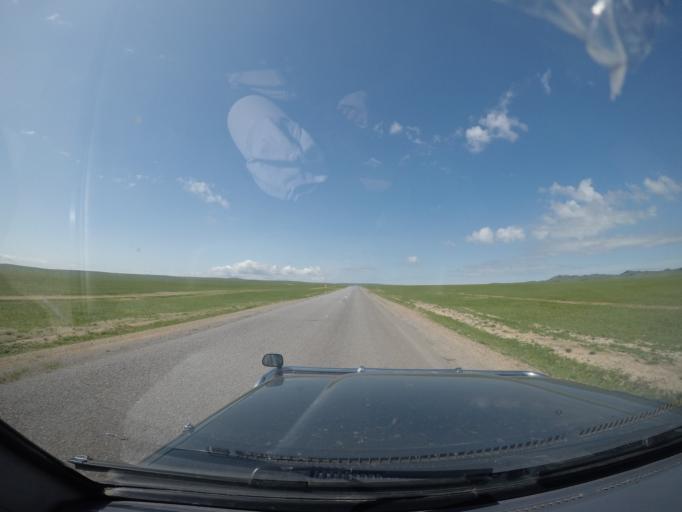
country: MN
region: Hentiy
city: Bayan
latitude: 47.3202
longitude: 111.4054
